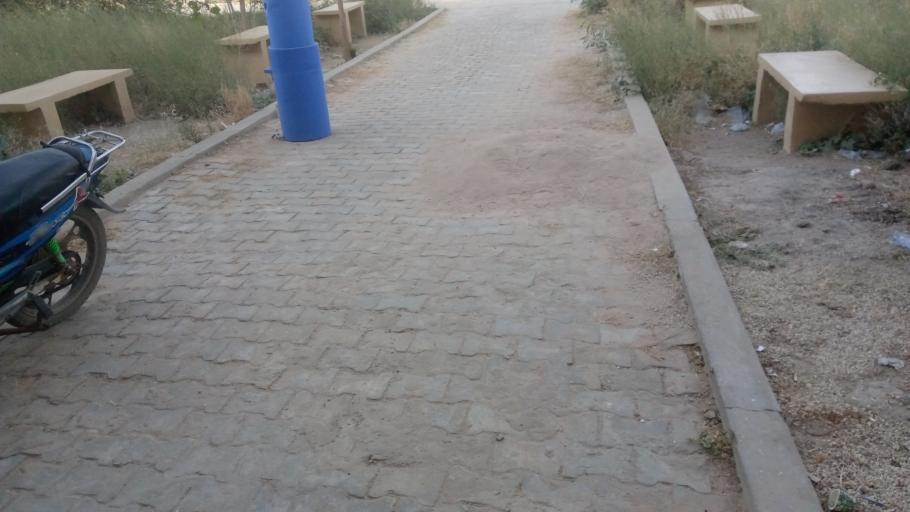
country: SN
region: Fatick
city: Guinguineo
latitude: 14.2238
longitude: -16.0599
